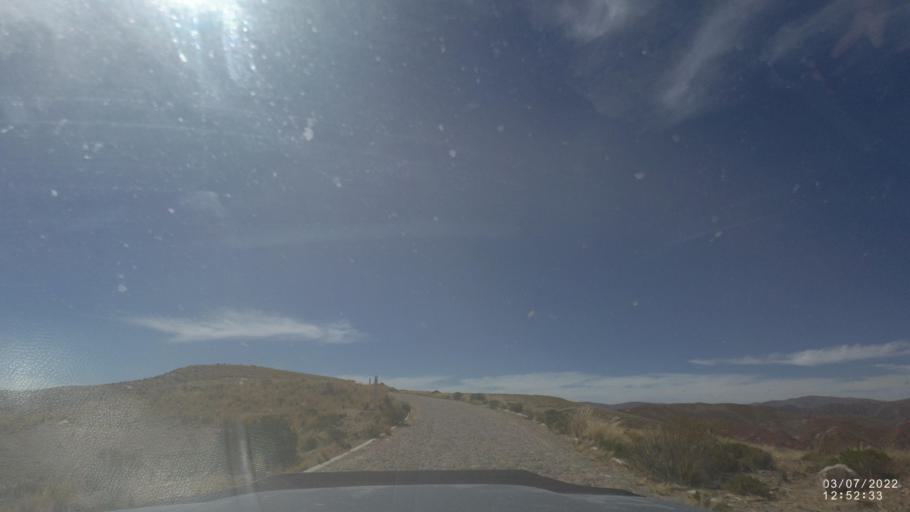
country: BO
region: Cochabamba
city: Irpa Irpa
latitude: -17.7496
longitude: -66.6616
